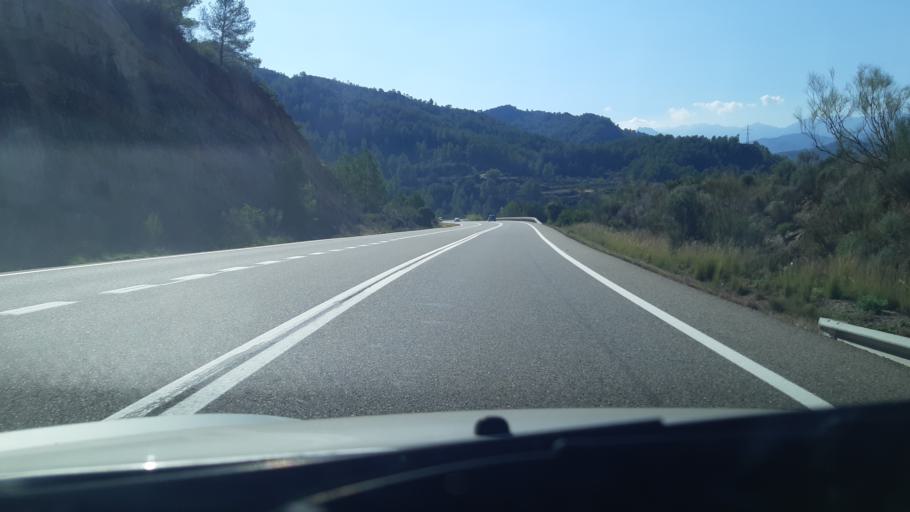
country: ES
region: Catalonia
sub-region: Provincia de Tarragona
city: Benifallet
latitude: 40.9851
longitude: 0.5374
